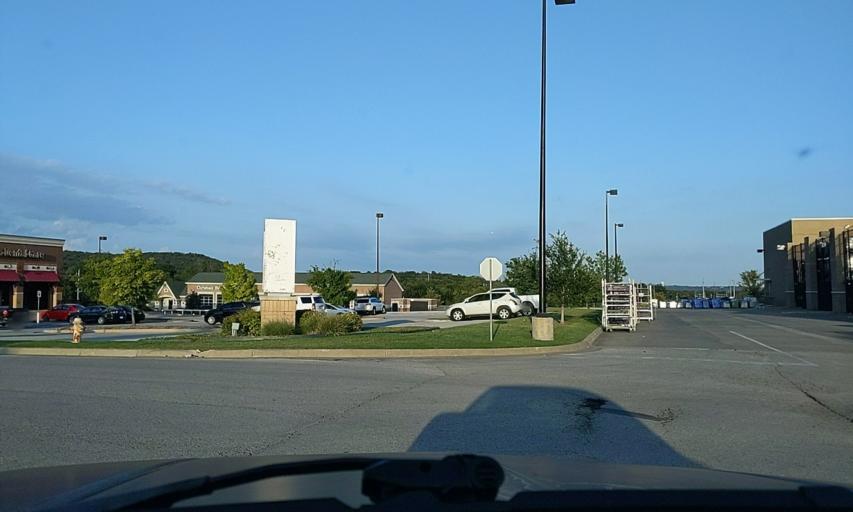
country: US
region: Oklahoma
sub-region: Tulsa County
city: Jenks
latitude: 36.0600
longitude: -96.0020
